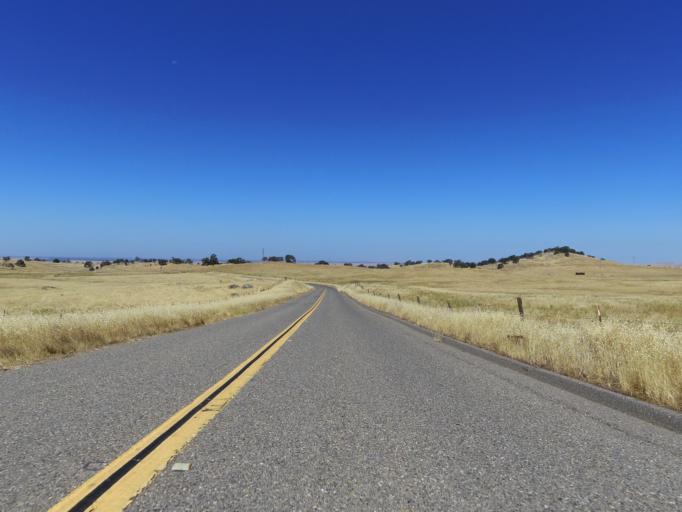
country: US
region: California
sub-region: Merced County
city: Planada
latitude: 37.5710
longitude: -120.3146
